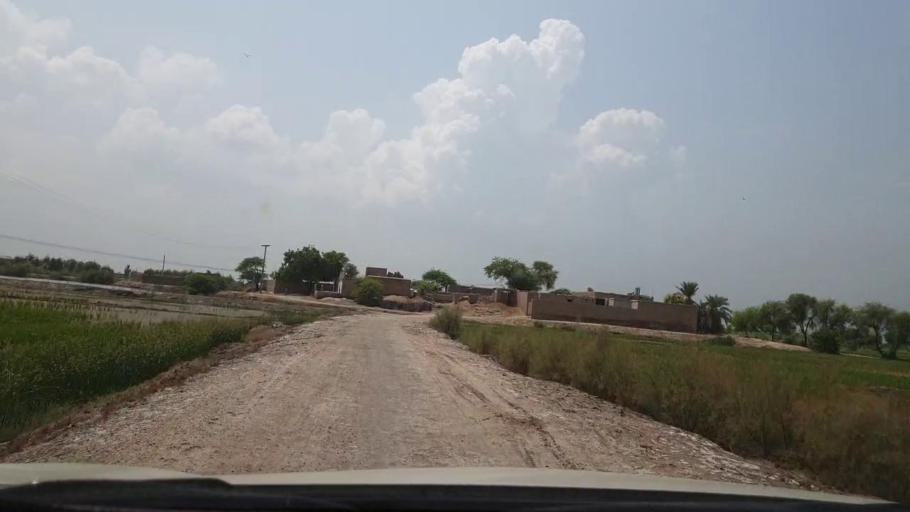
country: PK
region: Sindh
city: New Badah
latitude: 27.3889
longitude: 68.0420
